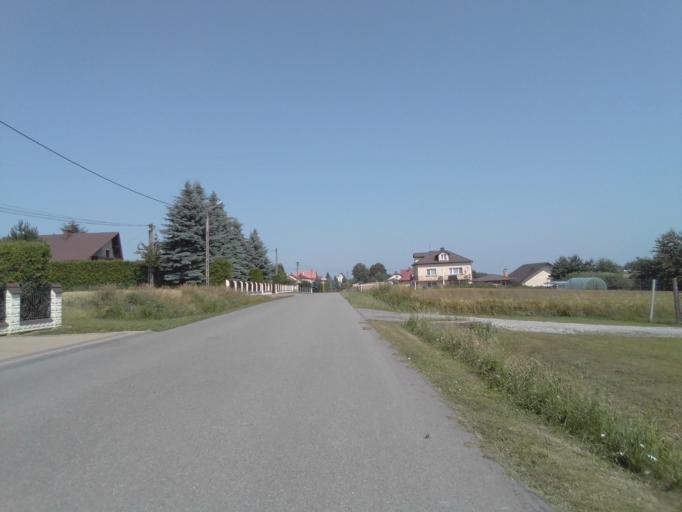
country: PL
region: Subcarpathian Voivodeship
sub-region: Powiat ropczycko-sedziszowski
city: Sedziszow Malopolski
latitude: 50.0597
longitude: 21.6665
